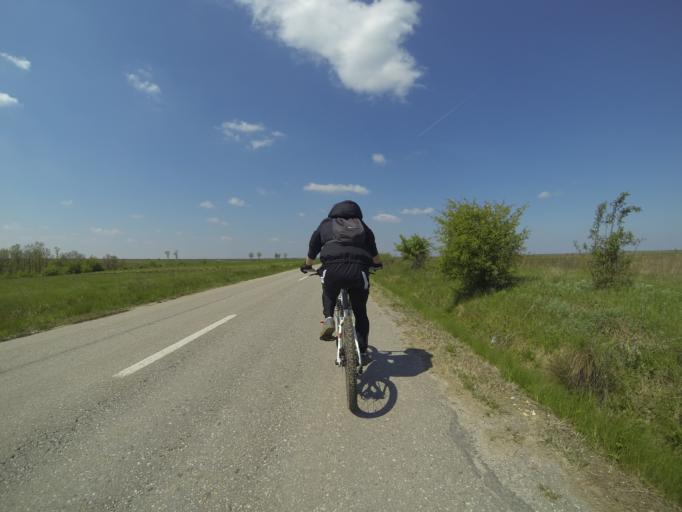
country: RO
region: Dolj
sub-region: Comuna Predesti
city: Predesti
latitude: 44.2998
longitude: 23.6190
